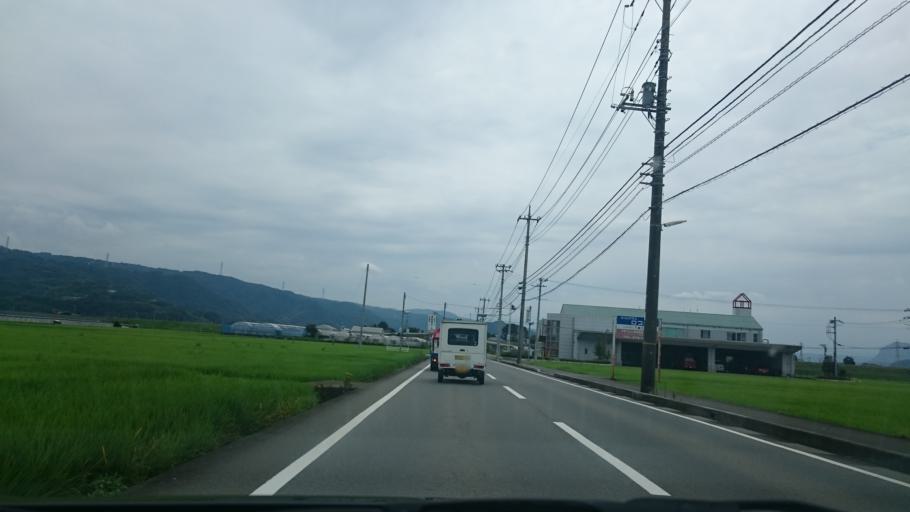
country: JP
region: Shizuoka
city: Mishima
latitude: 35.0754
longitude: 138.9483
